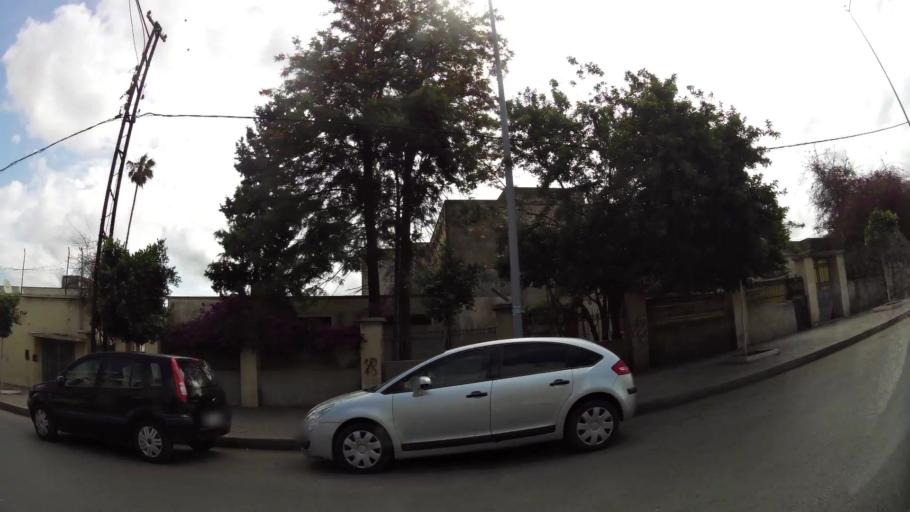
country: MA
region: Gharb-Chrarda-Beni Hssen
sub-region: Kenitra Province
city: Kenitra
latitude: 34.2650
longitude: -6.5707
